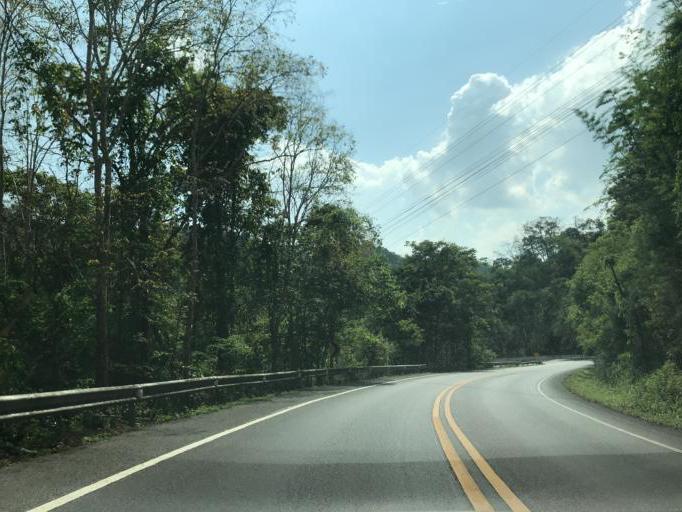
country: TH
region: Lampang
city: Wang Nuea
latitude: 19.0629
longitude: 99.7536
